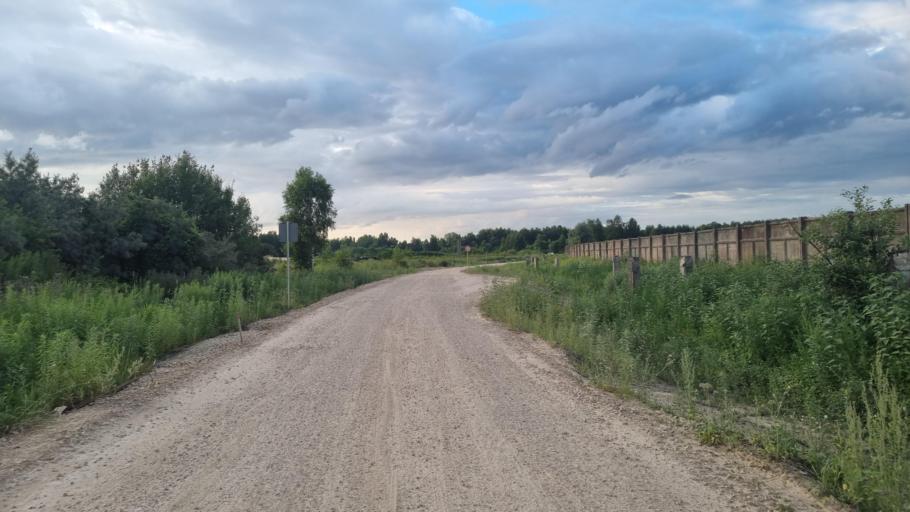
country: LV
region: Stopini
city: Ulbroka
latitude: 56.9153
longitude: 24.2390
